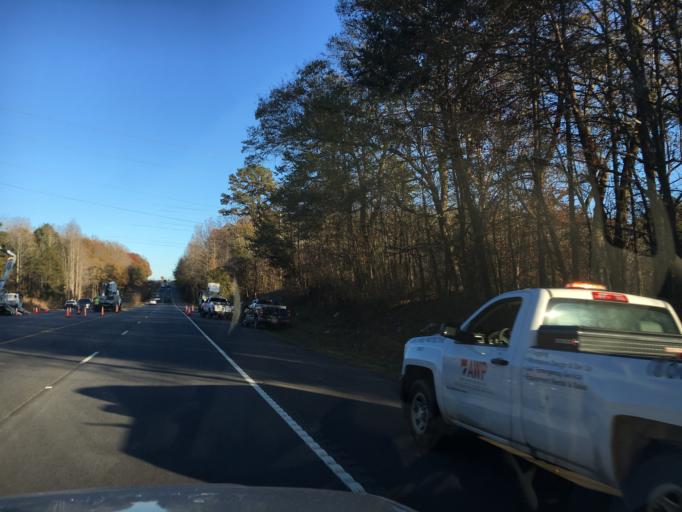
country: US
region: South Carolina
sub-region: Spartanburg County
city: Duncan
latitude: 34.9555
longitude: -82.1554
